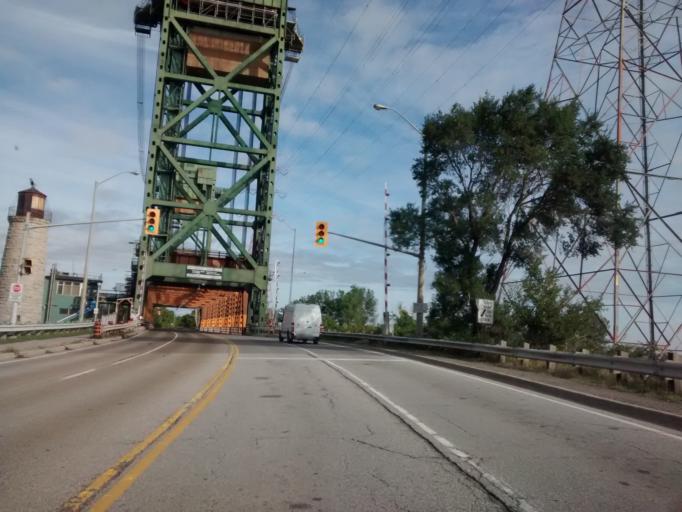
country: CA
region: Ontario
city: Hamilton
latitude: 43.2978
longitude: -79.7946
